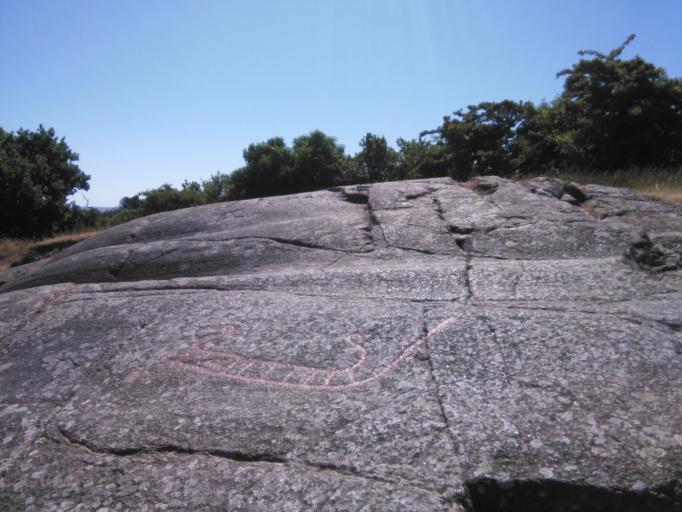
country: DK
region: Capital Region
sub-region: Bornholm Kommune
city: Ronne
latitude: 55.2819
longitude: 14.7889
